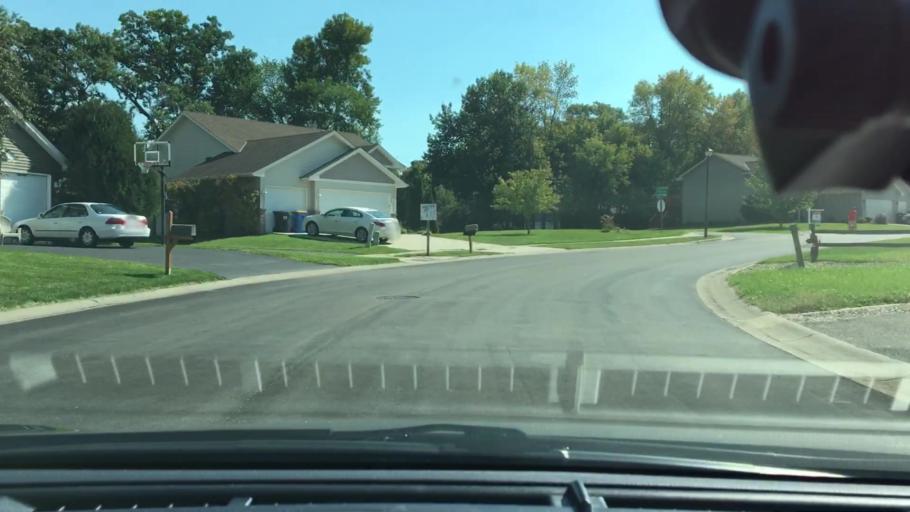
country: US
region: Minnesota
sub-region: Wright County
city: Saint Michael
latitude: 45.2044
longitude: -93.6760
